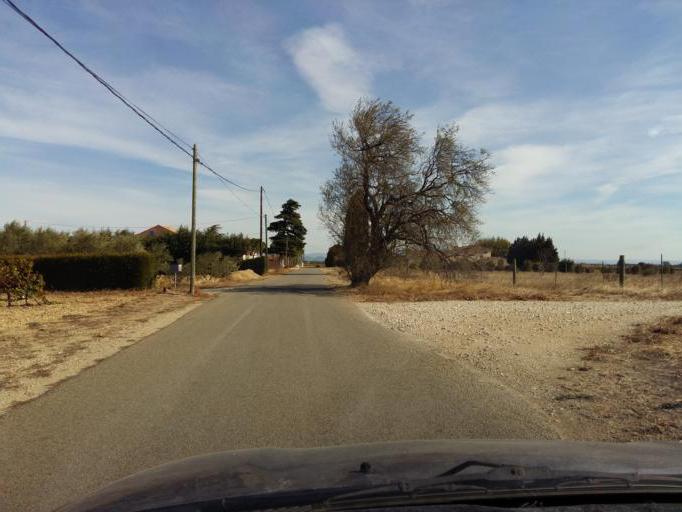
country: FR
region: Provence-Alpes-Cote d'Azur
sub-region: Departement du Vaucluse
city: Piolenc
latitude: 44.1783
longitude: 4.7811
